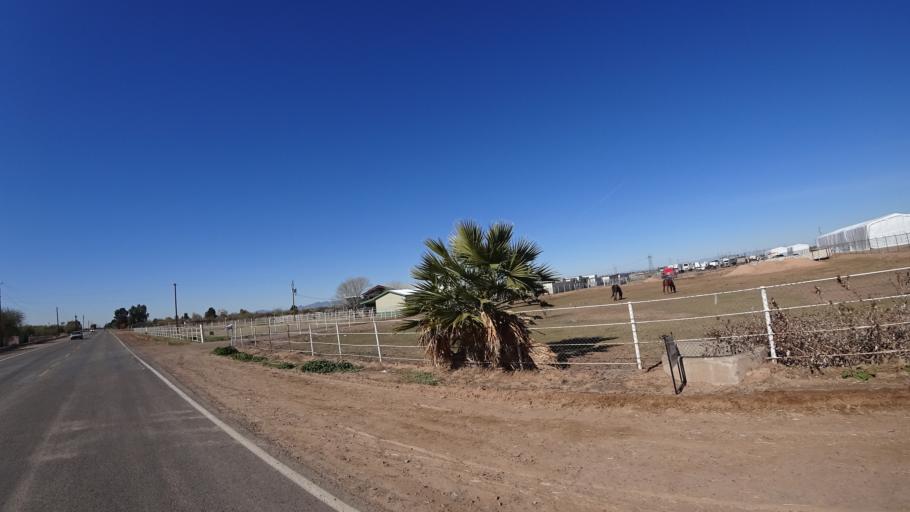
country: US
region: Arizona
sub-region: Maricopa County
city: Avondale
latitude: 33.3918
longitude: -112.3190
